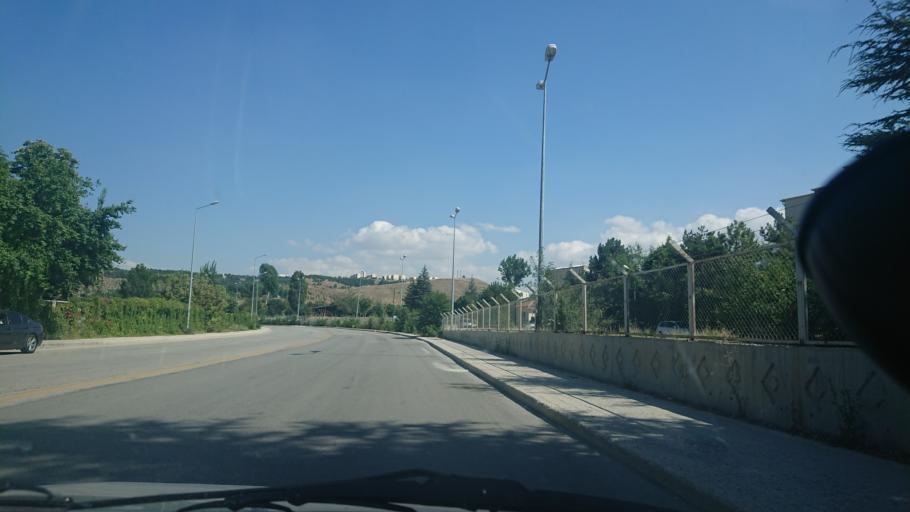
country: TR
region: Ankara
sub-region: Goelbasi
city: Golbasi
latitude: 39.8070
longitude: 32.8192
